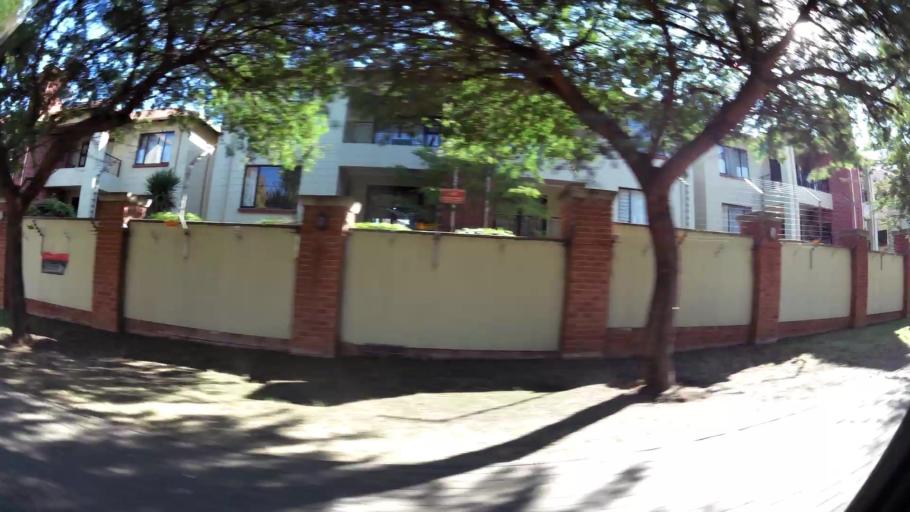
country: ZA
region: Gauteng
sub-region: City of Johannesburg Metropolitan Municipality
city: Midrand
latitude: -26.0214
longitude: 28.0623
